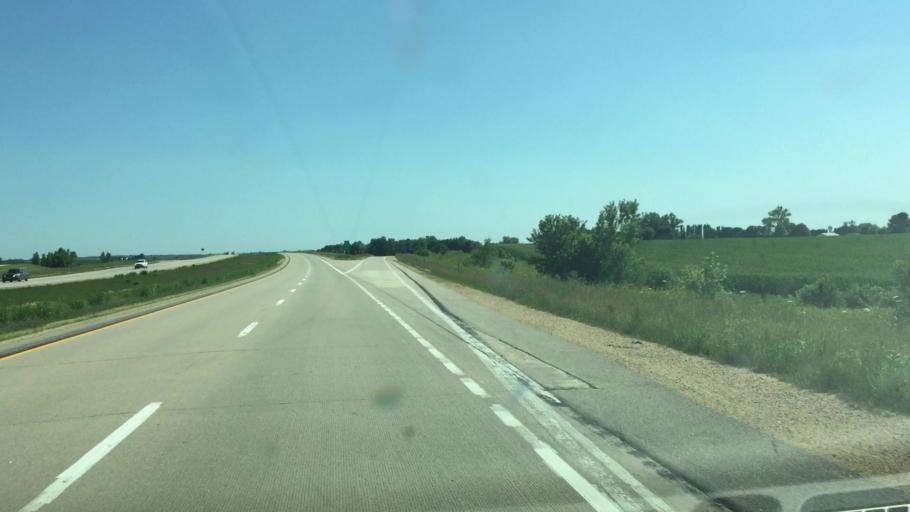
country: US
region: Iowa
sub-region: Jones County
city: Monticello
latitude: 42.2370
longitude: -91.1694
